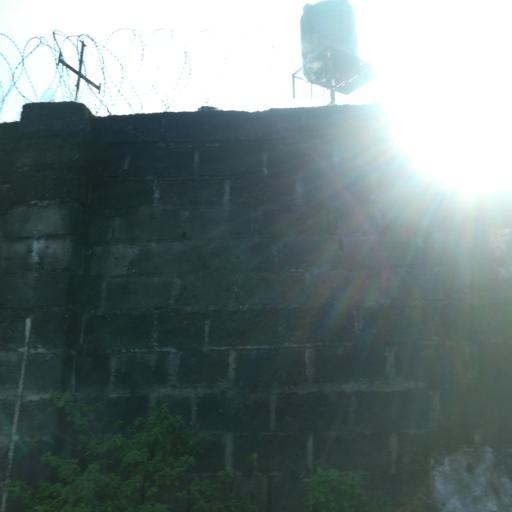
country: NG
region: Rivers
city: Port Harcourt
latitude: 4.8078
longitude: 7.0186
